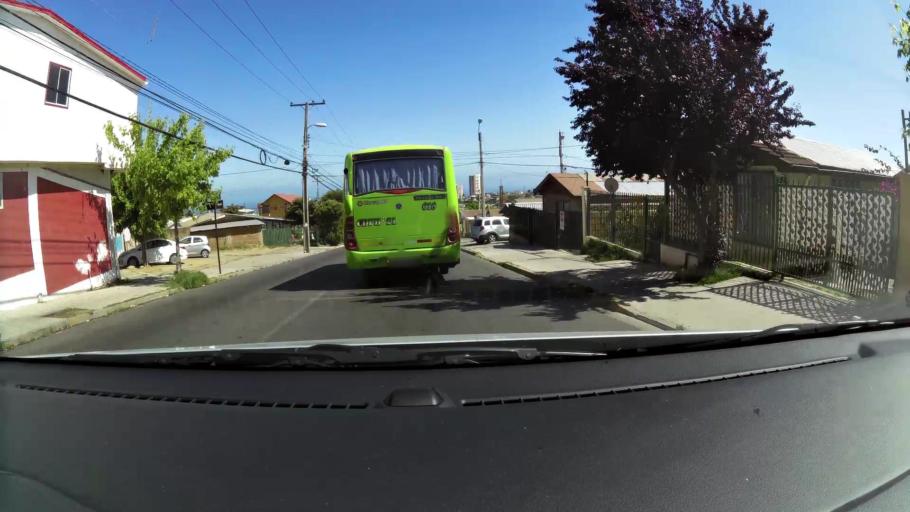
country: CL
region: Valparaiso
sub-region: Provincia de Valparaiso
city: Vina del Mar
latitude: -33.0581
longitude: -71.5766
